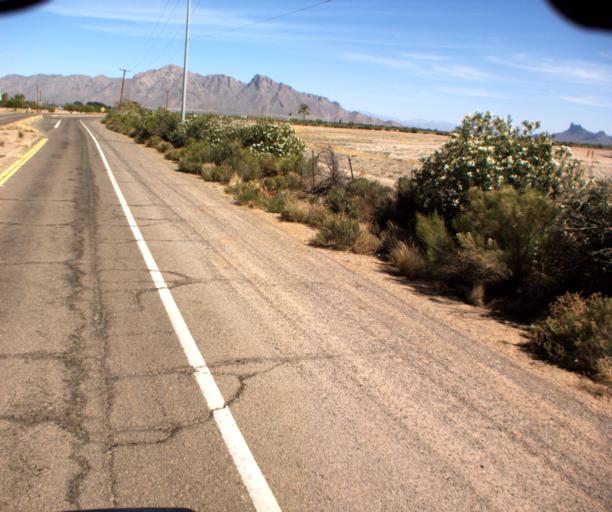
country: US
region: Arizona
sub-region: Pinal County
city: Eloy
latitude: 32.7341
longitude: -111.5204
